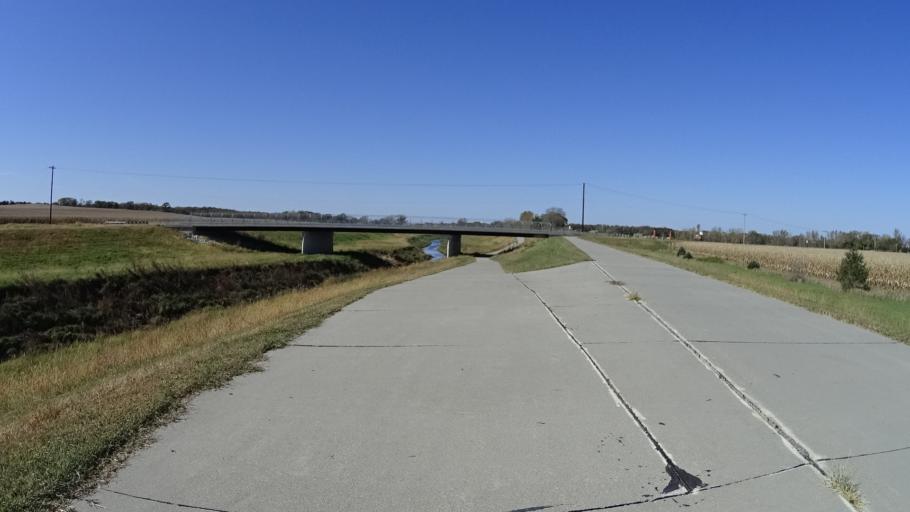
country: US
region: Nebraska
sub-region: Sarpy County
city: Papillion
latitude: 41.1492
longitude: -95.9844
